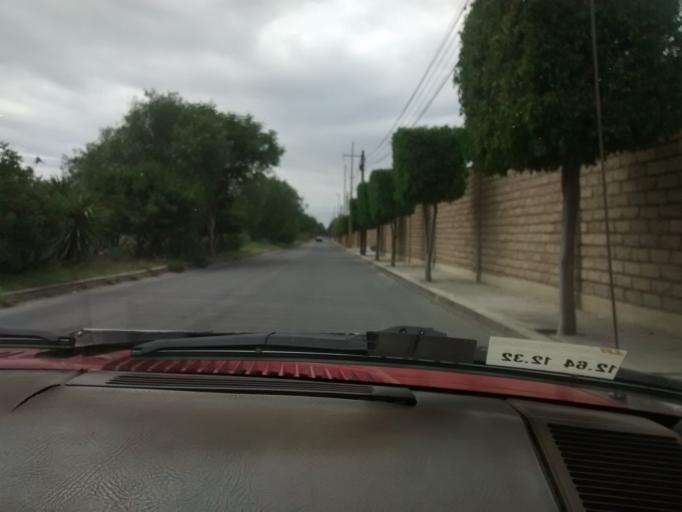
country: MX
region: Puebla
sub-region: Santiago Miahuatlan
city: San Isidro Vista Hermosa
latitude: 18.4816
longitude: -97.4127
